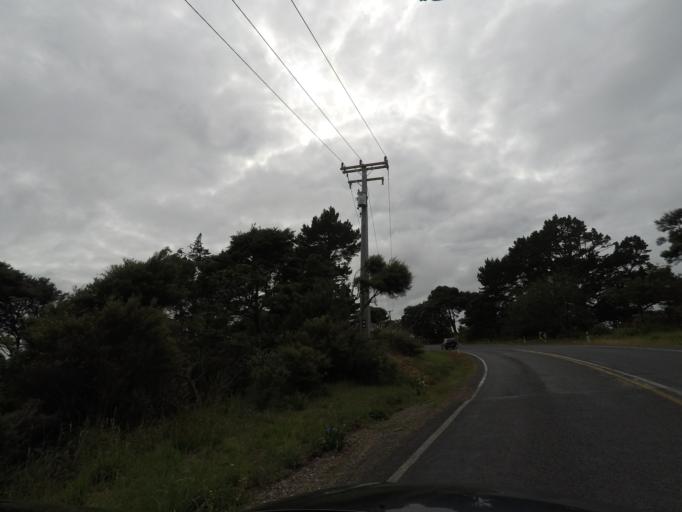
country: NZ
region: Auckland
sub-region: Auckland
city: Rosebank
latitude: -36.8380
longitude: 174.5833
